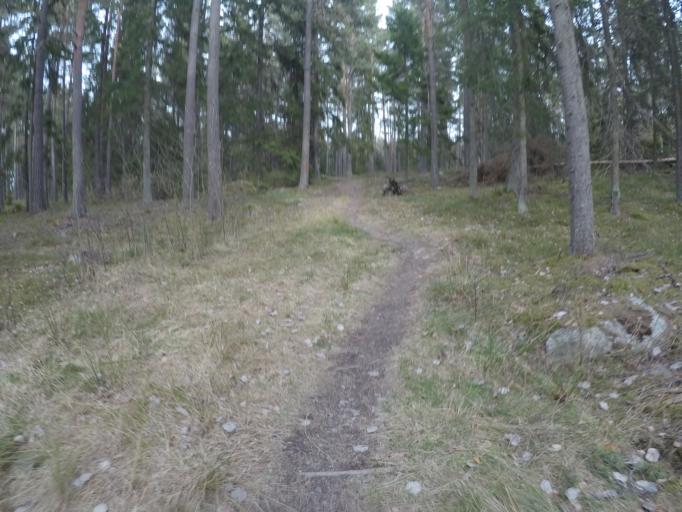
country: SE
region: Soedermanland
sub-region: Eskilstuna Kommun
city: Torshalla
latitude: 59.4361
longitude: 16.5080
